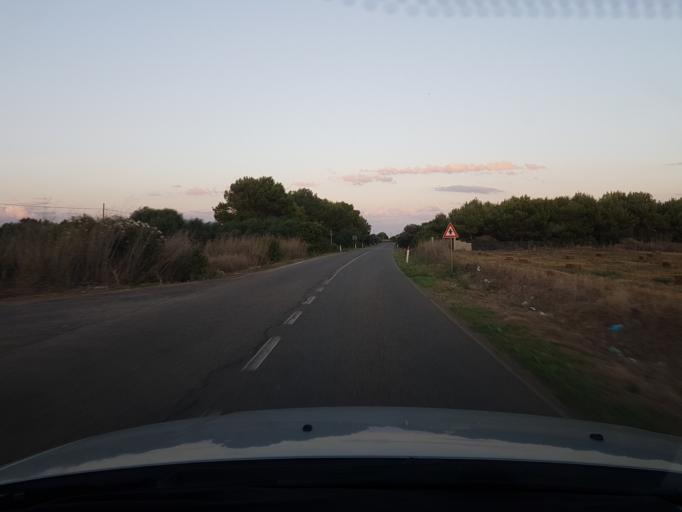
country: IT
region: Sardinia
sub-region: Provincia di Oristano
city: Riola Sardo
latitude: 40.0279
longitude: 8.4253
